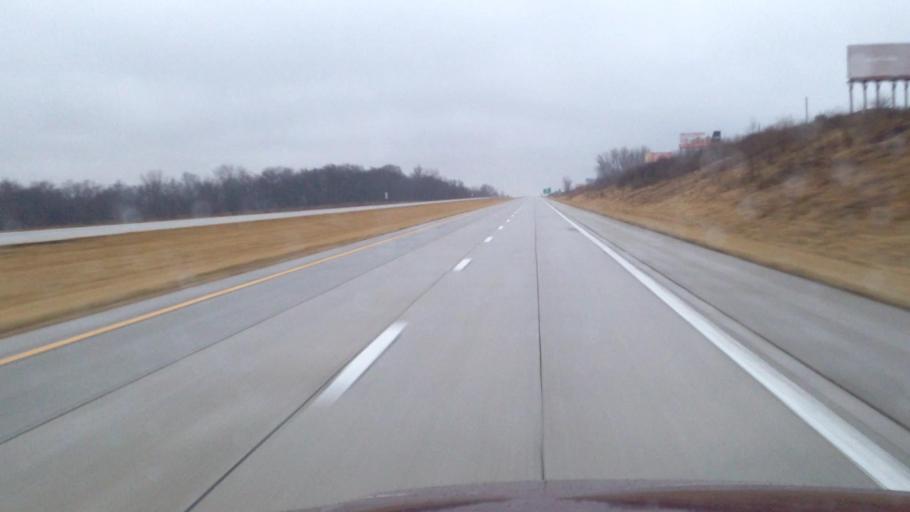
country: US
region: Missouri
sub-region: Daviess County
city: Gallatin
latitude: 40.0537
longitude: -94.0943
